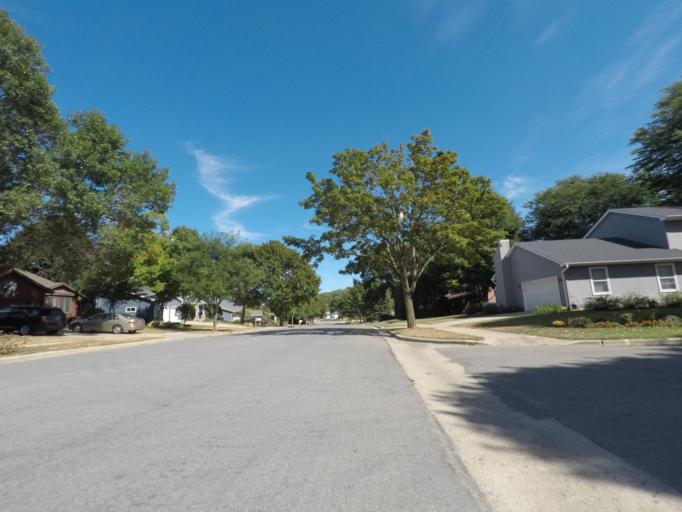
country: US
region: Wisconsin
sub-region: Dane County
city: Middleton
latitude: 43.0812
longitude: -89.5045
